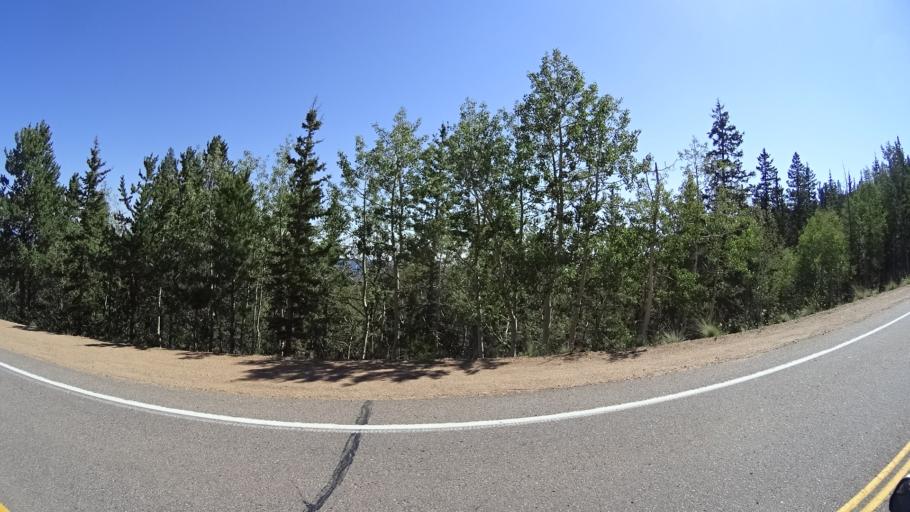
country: US
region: Colorado
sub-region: El Paso County
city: Cascade-Chipita Park
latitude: 38.8958
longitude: -105.0634
